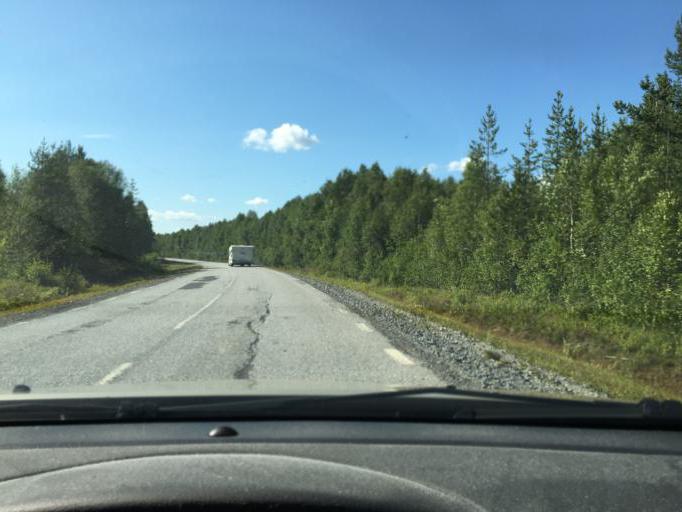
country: SE
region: Norrbotten
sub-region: Lulea Kommun
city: Ranea
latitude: 66.0478
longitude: 22.2762
